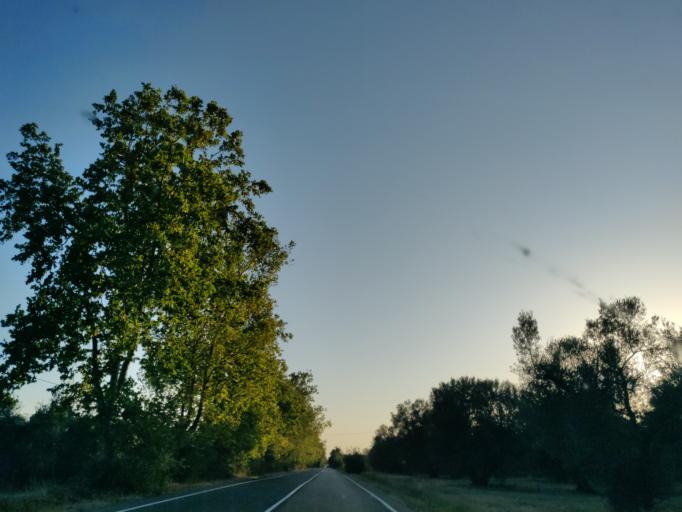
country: IT
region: Latium
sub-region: Provincia di Viterbo
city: Canino
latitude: 42.4000
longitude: 11.6878
